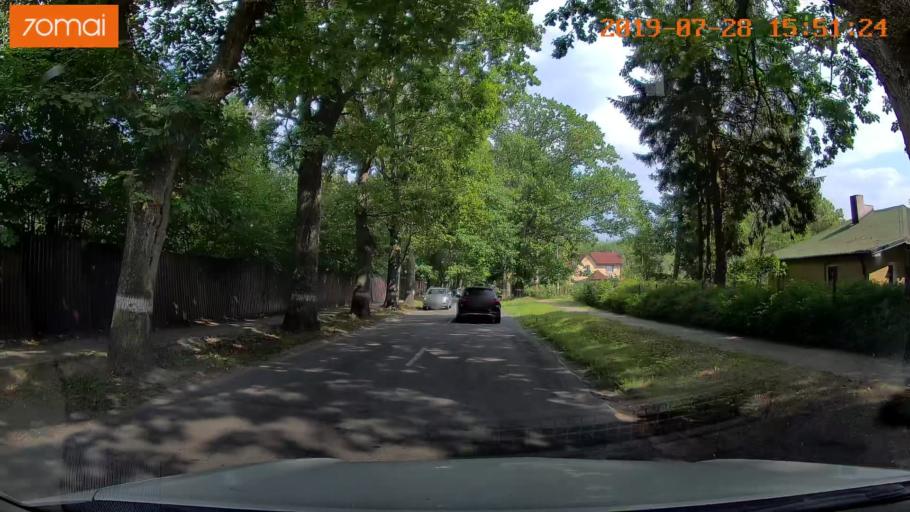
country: RU
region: Kaliningrad
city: Otradnoye
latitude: 54.9413
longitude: 20.1046
